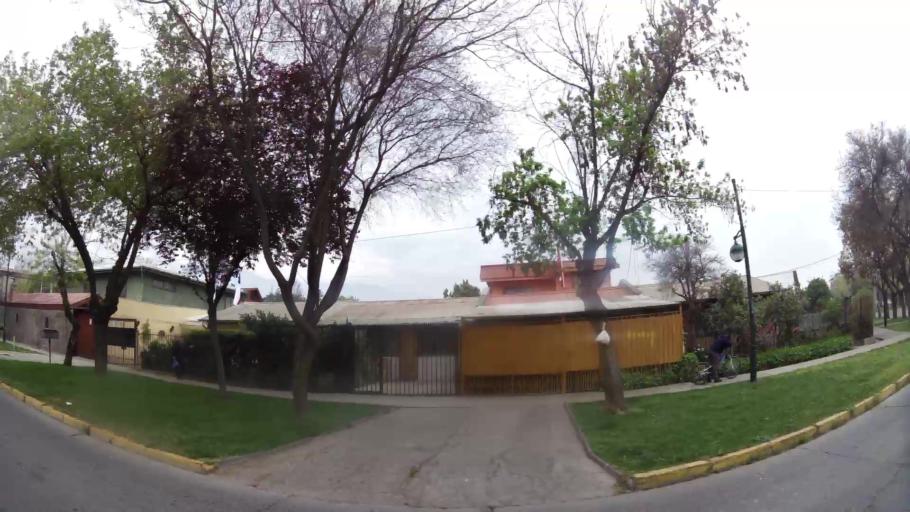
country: CL
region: Santiago Metropolitan
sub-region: Provincia de Santiago
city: Villa Presidente Frei, Nunoa, Santiago, Chile
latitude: -33.4722
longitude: -70.5920
